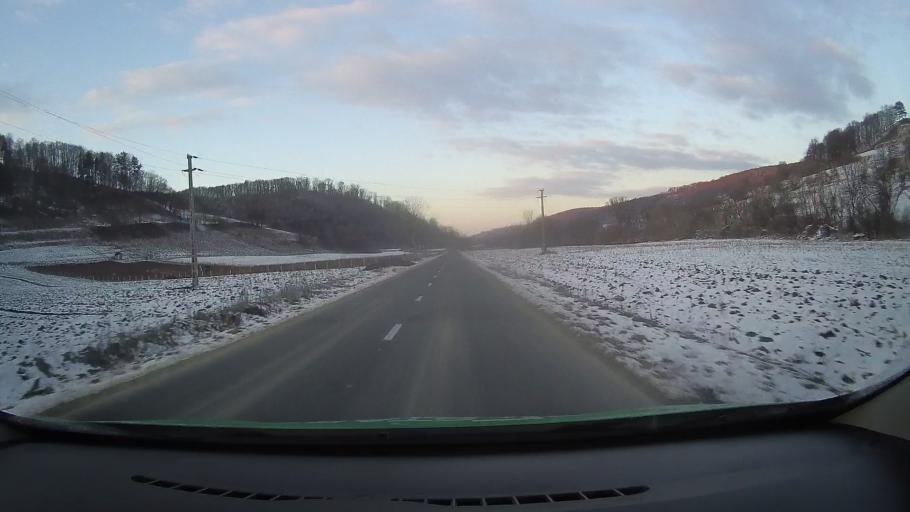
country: RO
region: Sibiu
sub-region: Comuna Atel
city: Atel
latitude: 46.1693
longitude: 24.4681
